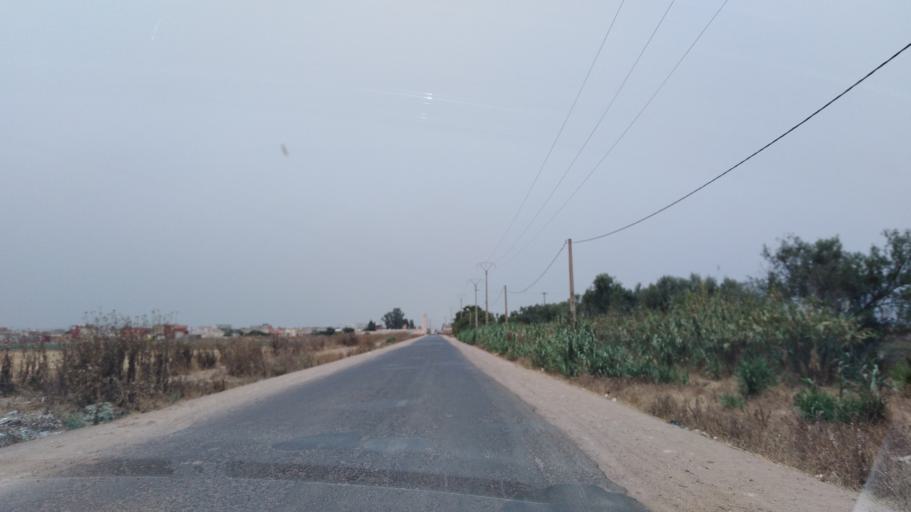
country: MA
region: Grand Casablanca
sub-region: Mediouna
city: Mediouna
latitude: 33.4111
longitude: -7.5150
